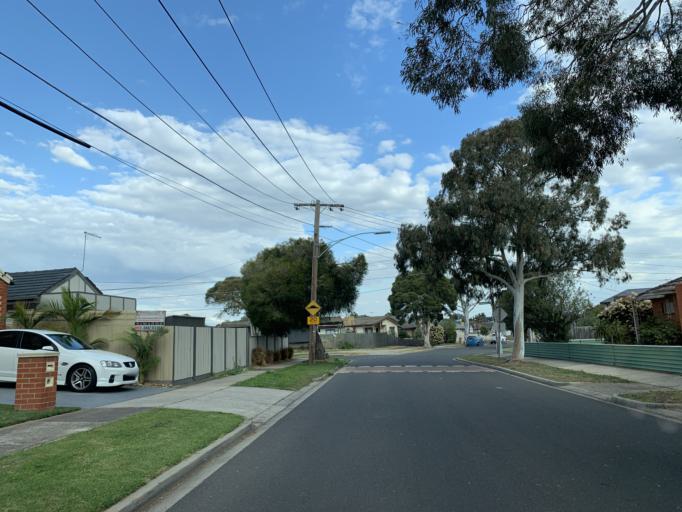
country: AU
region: Victoria
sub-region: Brimbank
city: Albion
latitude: -37.7578
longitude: 144.8533
